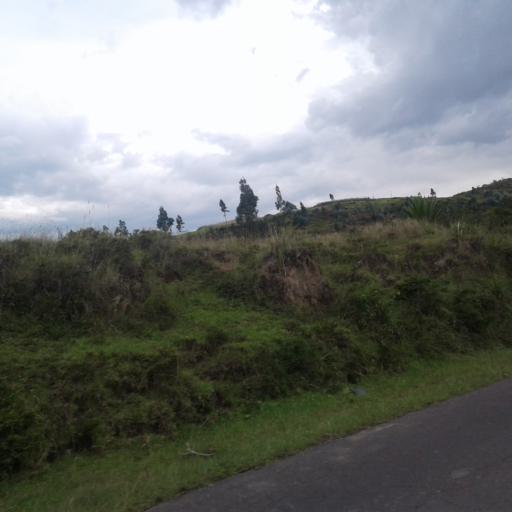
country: EC
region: Pichincha
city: Sangolqui
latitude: -0.2885
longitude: -78.3870
